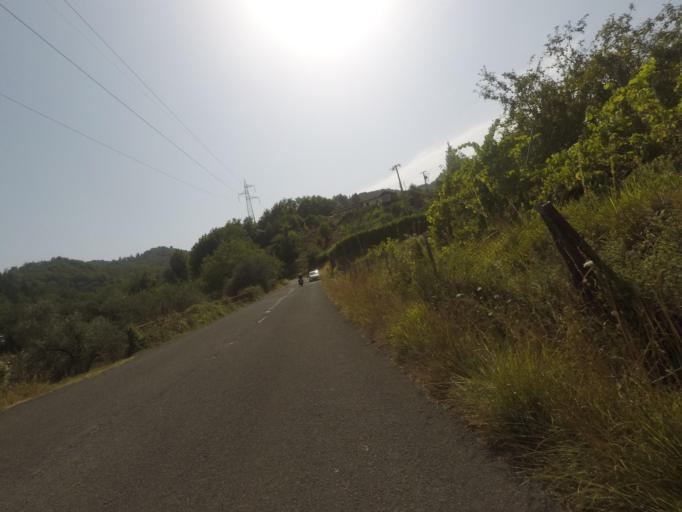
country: IT
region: Tuscany
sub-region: Provincia di Massa-Carrara
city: Fivizzano
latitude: 44.1714
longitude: 10.1093
